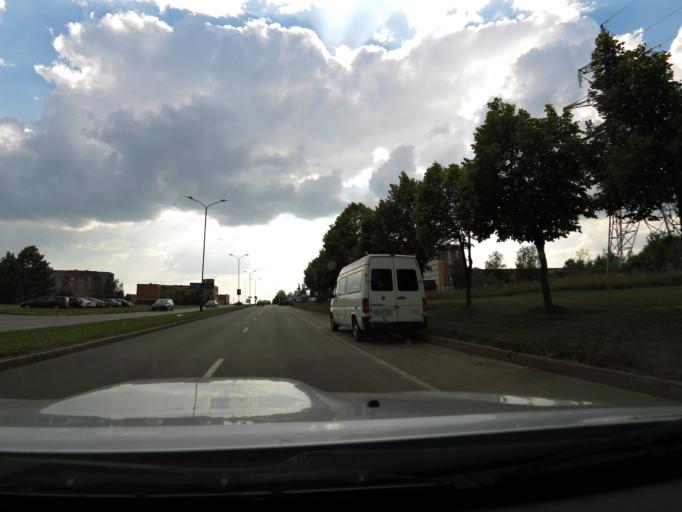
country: LT
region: Siauliu apskritis
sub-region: Siauliai
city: Siauliai
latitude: 55.9165
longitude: 23.2491
